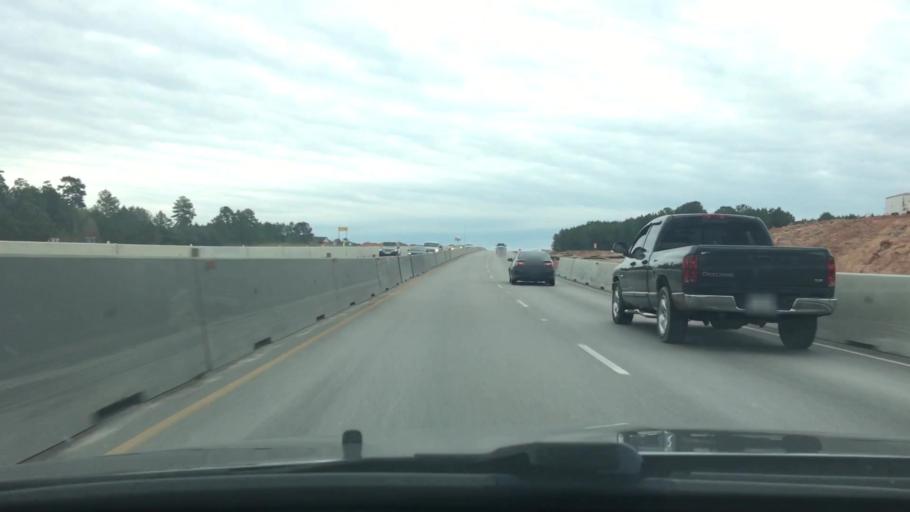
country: US
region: Texas
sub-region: Walker County
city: Huntsville
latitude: 30.6803
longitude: -95.5265
